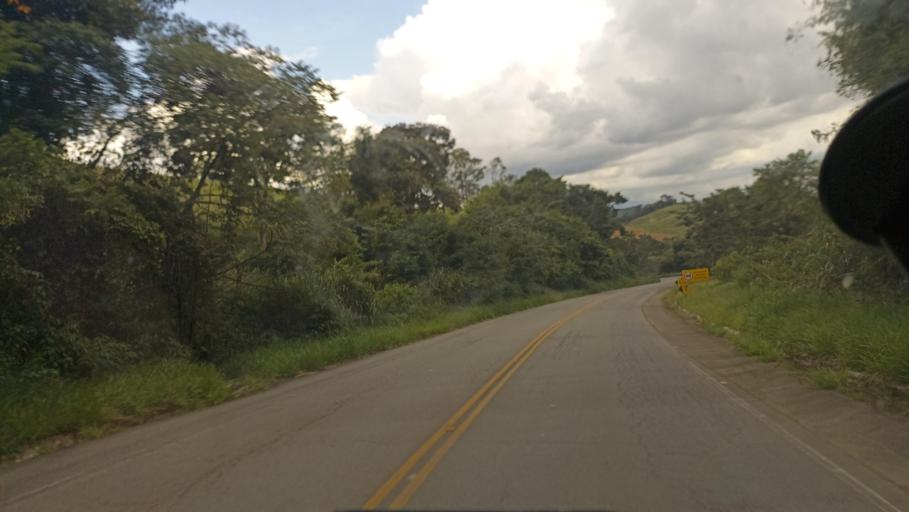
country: BR
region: Minas Gerais
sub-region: Cruzilia
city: Cruzilia
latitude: -21.8752
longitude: -44.8137
